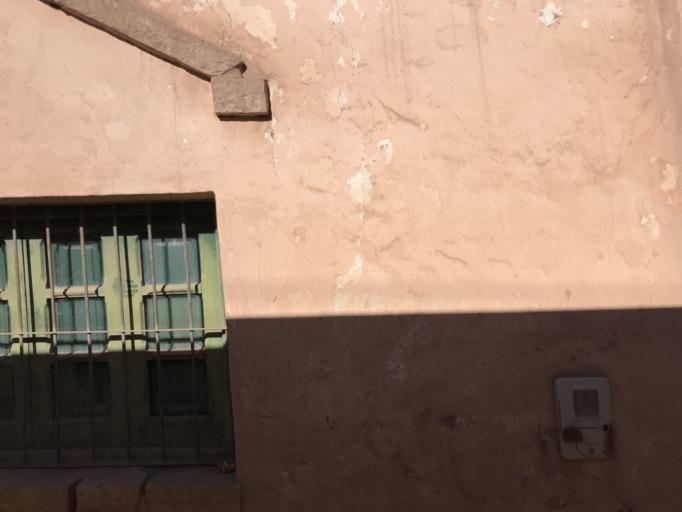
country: AR
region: Jujuy
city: Maimara
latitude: -23.6271
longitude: -65.4090
